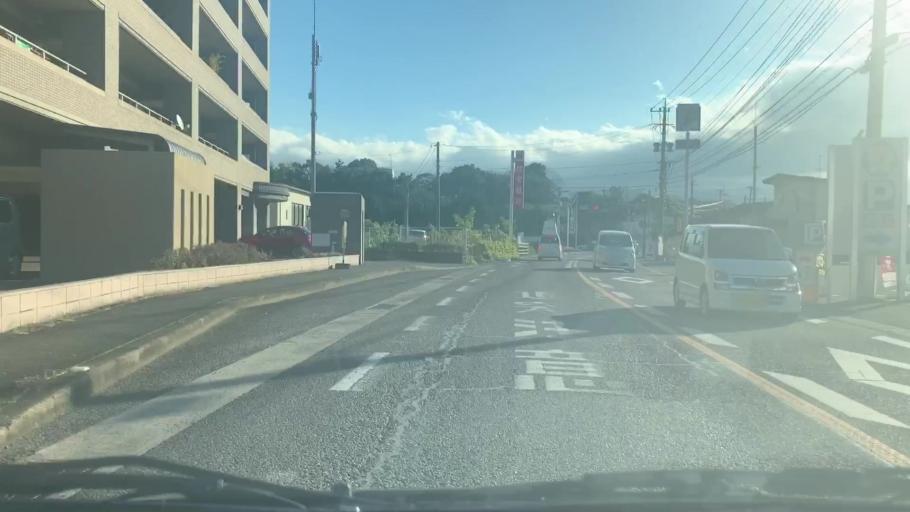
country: JP
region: Saga Prefecture
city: Takeocho-takeo
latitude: 33.2205
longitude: 130.0724
